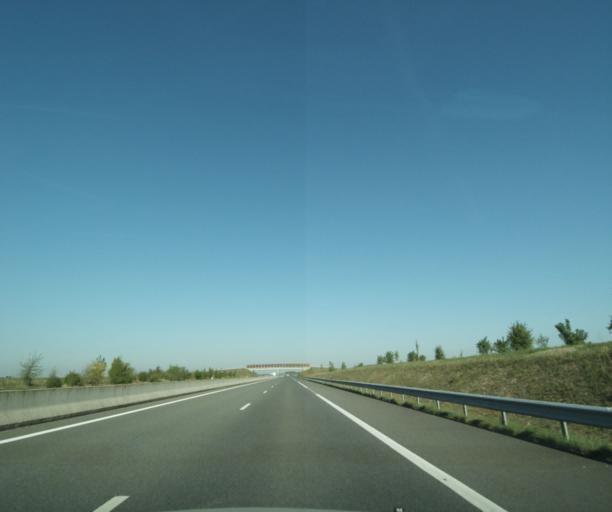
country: FR
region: Centre
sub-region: Departement du Loiret
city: Pannes
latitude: 48.0703
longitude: 2.6453
